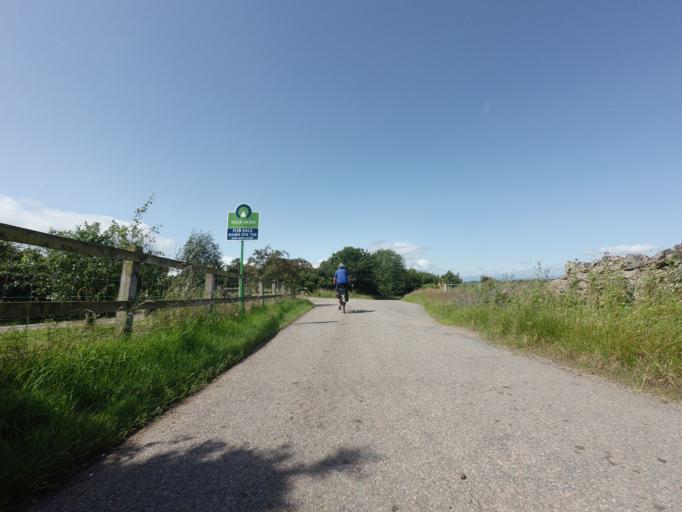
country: GB
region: Scotland
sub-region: Highland
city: Nairn
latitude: 57.5035
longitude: -3.9868
